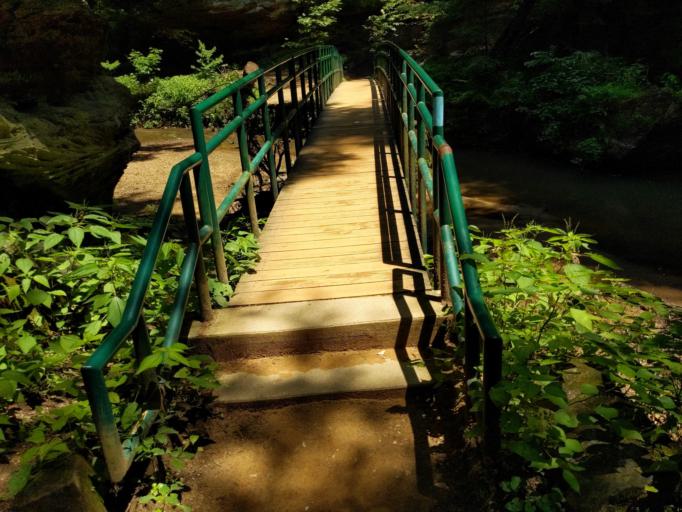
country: US
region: Ohio
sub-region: Hocking County
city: Logan
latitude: 39.4344
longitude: -82.5406
